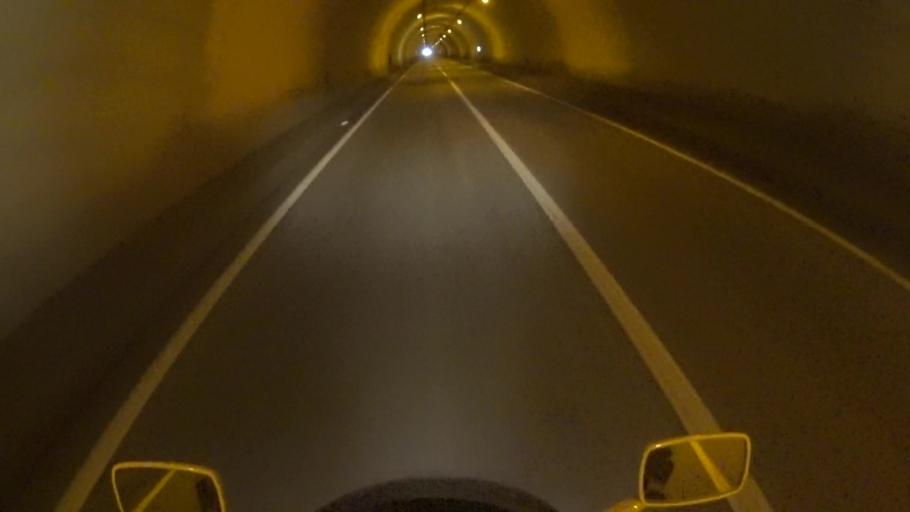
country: JP
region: Kyoto
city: Maizuru
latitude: 35.5181
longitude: 135.3709
